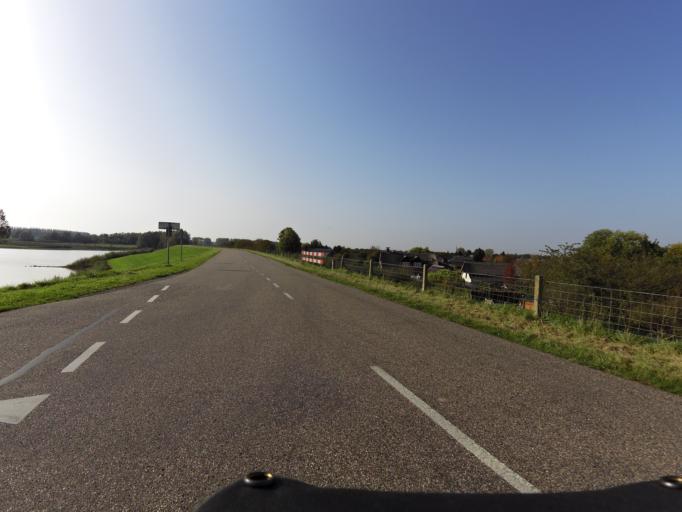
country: NL
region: Gelderland
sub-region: Gemeente Groesbeek
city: Berg en Dal
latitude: 51.8687
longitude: 5.9580
